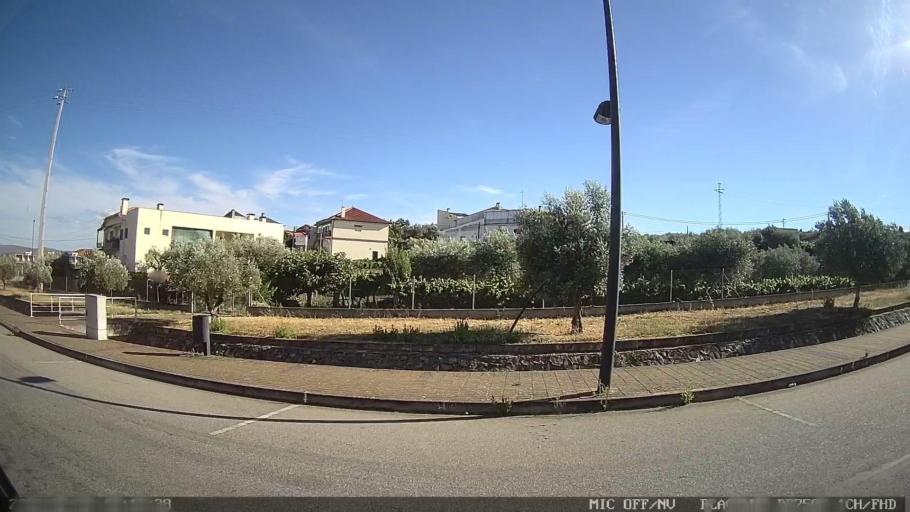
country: PT
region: Vila Real
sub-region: Murca
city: Murca
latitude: 41.4098
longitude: -7.4536
